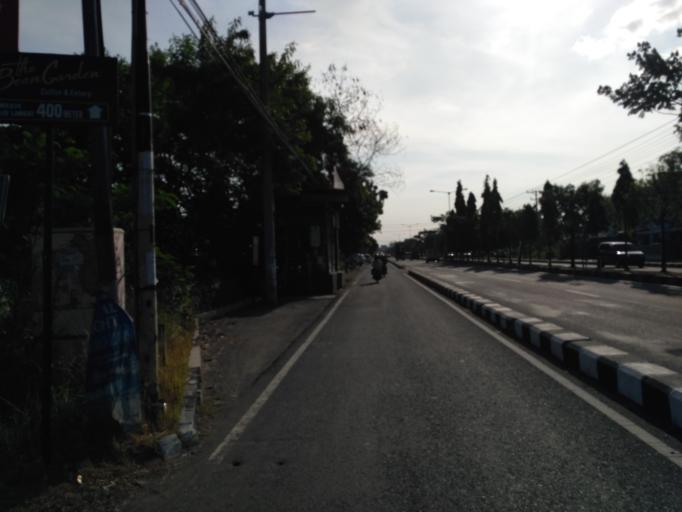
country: ID
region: Daerah Istimewa Yogyakarta
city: Depok
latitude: -7.7643
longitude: 110.4236
